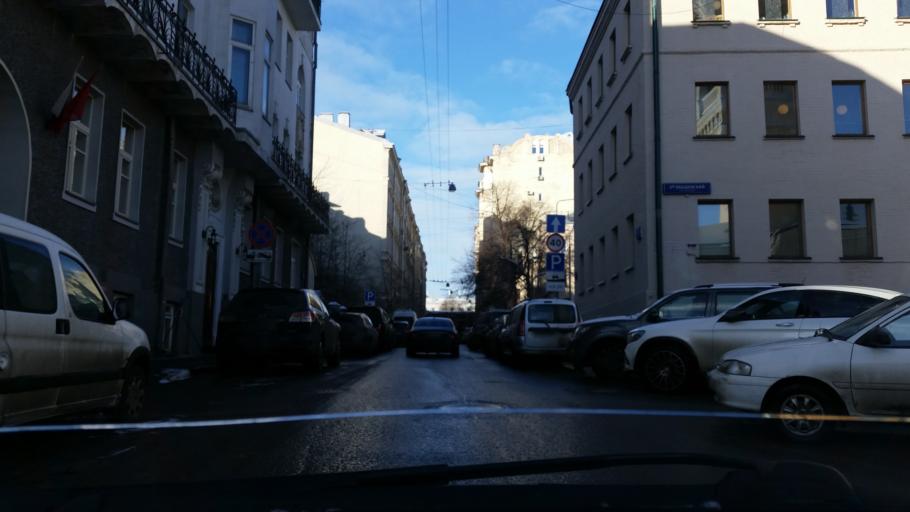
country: RU
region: Moscow
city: Moscow
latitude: 55.7421
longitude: 37.6034
